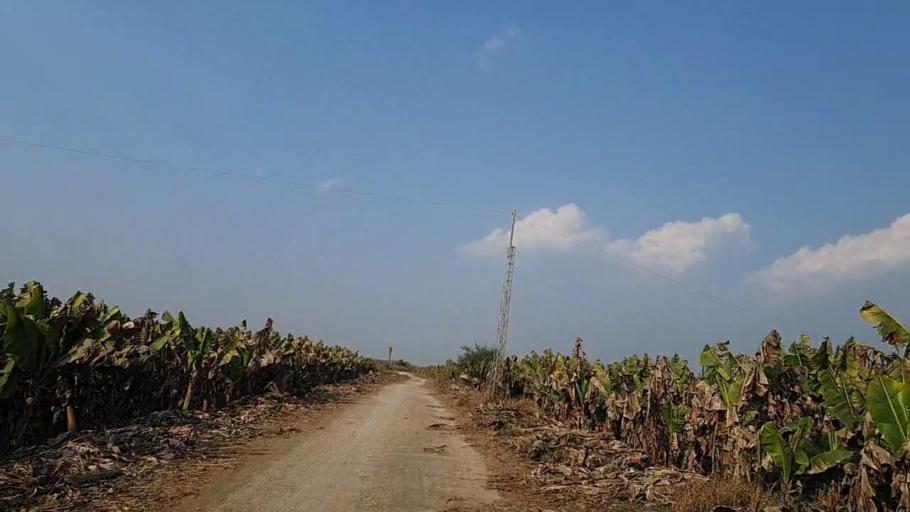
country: PK
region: Sindh
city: Nawabshah
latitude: 26.1501
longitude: 68.4005
